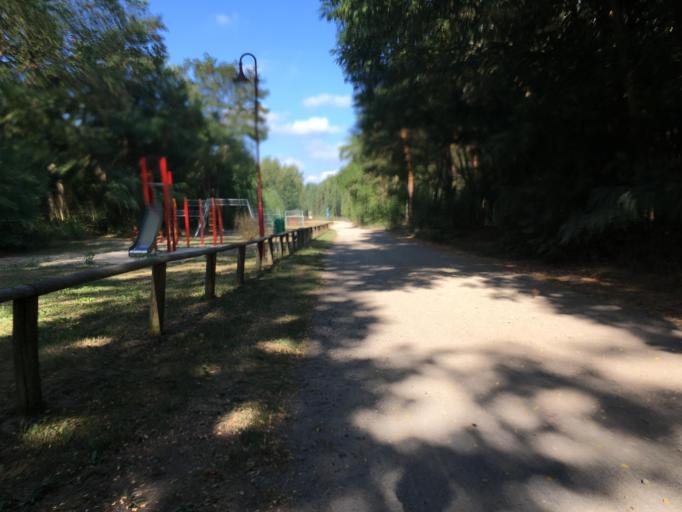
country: DE
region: Brandenburg
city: Liebenwalde
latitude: 52.9137
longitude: 13.4575
